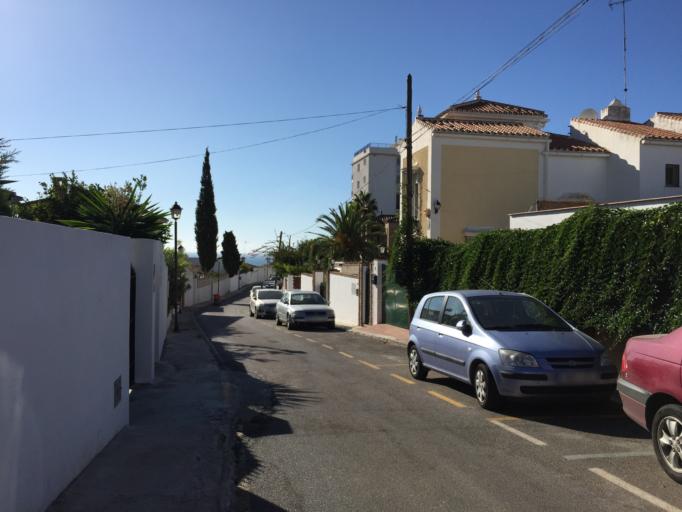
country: ES
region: Andalusia
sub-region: Provincia de Malaga
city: Nerja
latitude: 36.7535
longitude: -3.8722
